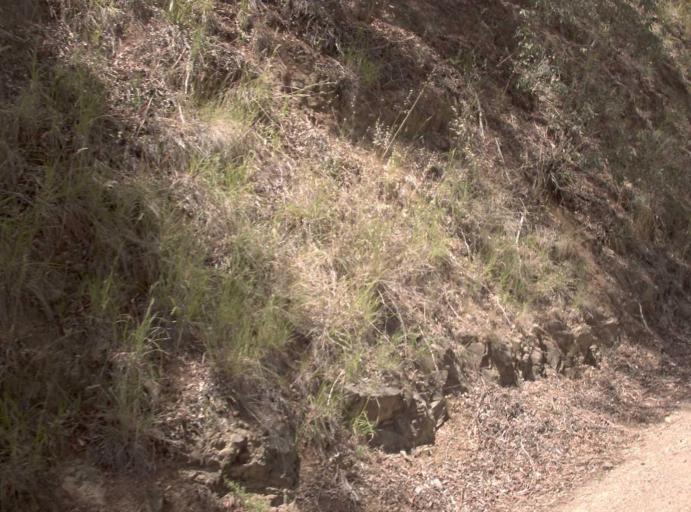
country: AU
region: Victoria
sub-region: East Gippsland
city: Bairnsdale
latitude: -37.3725
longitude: 147.8373
